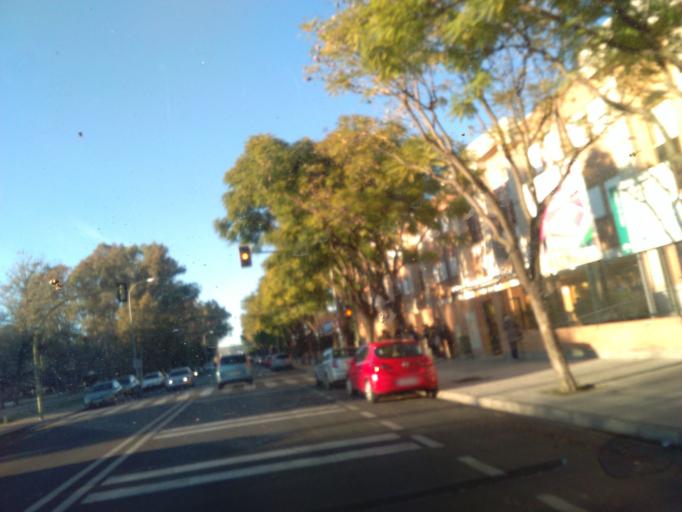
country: ES
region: Andalusia
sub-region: Provincia de Sevilla
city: Sevilla
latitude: 37.3978
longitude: -5.9305
